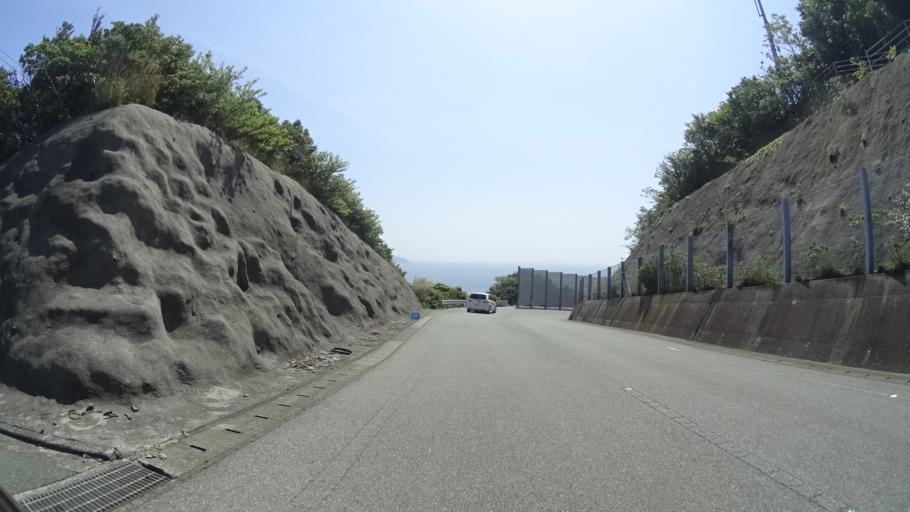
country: JP
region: Ehime
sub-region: Nishiuwa-gun
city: Ikata-cho
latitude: 33.3663
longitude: 132.0430
